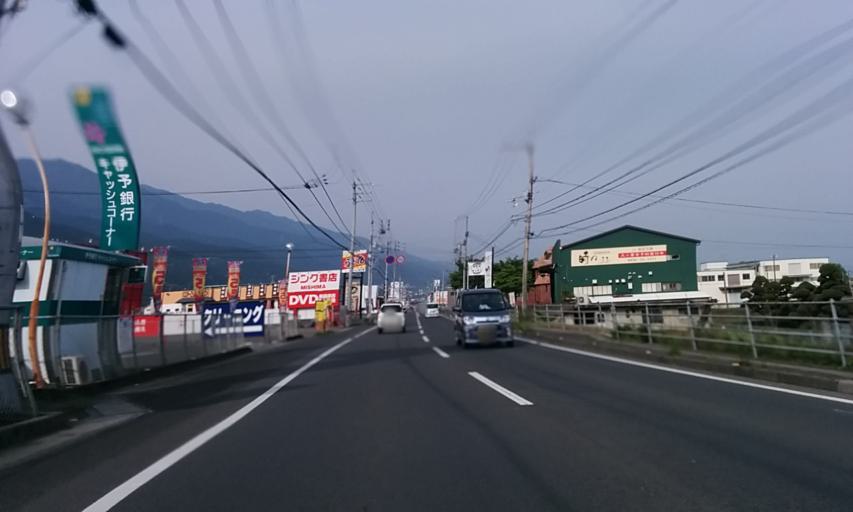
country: JP
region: Ehime
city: Kawanoecho
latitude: 33.9707
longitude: 133.5231
